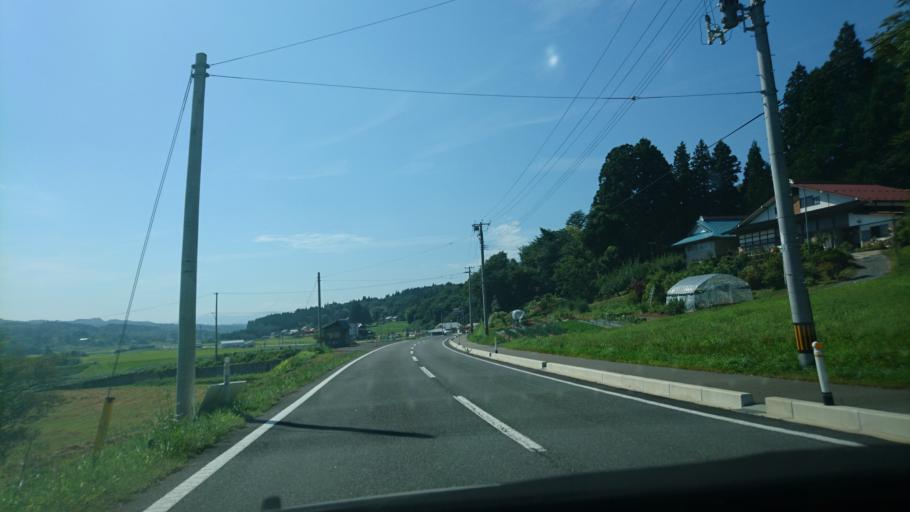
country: JP
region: Iwate
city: Ofunato
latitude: 39.0147
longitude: 141.4230
